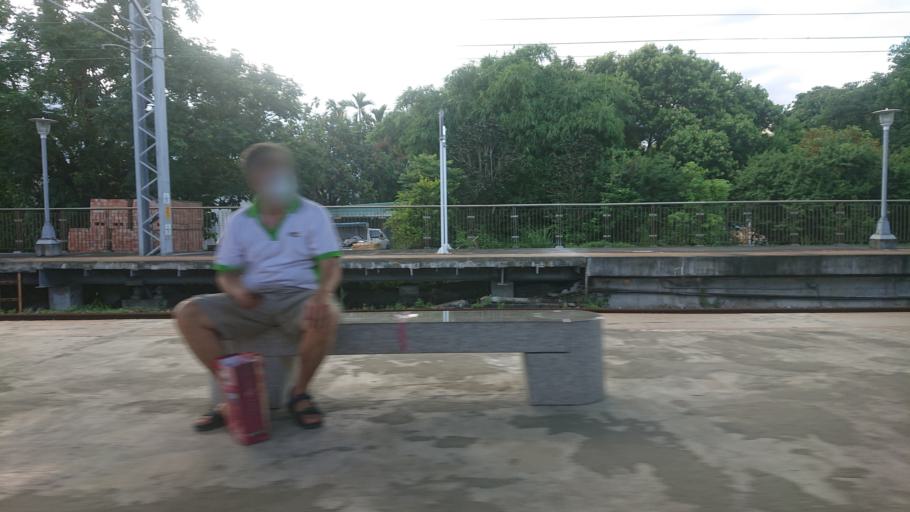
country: TW
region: Taiwan
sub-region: Hualien
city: Hualian
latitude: 23.9669
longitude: 121.5812
